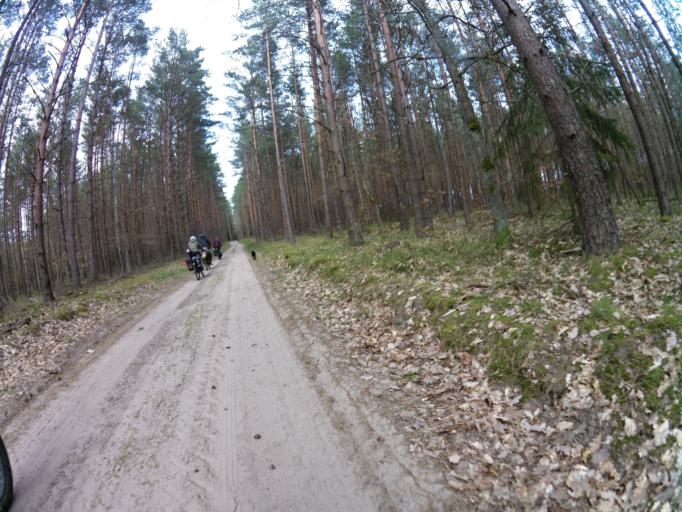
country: PL
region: West Pomeranian Voivodeship
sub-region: Powiat szczecinecki
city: Szczecinek
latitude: 53.8240
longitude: 16.6514
